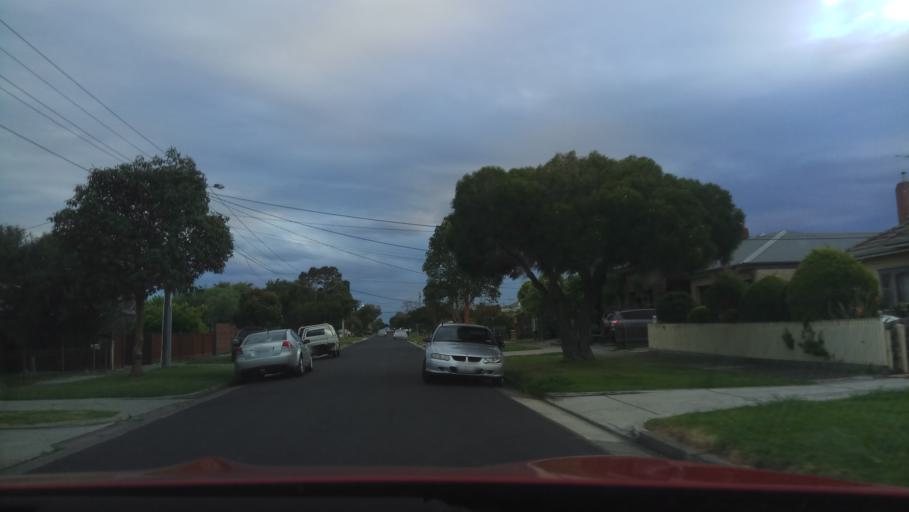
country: AU
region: Victoria
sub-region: Hobsons Bay
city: Seaholme
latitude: -37.8657
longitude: 144.8376
